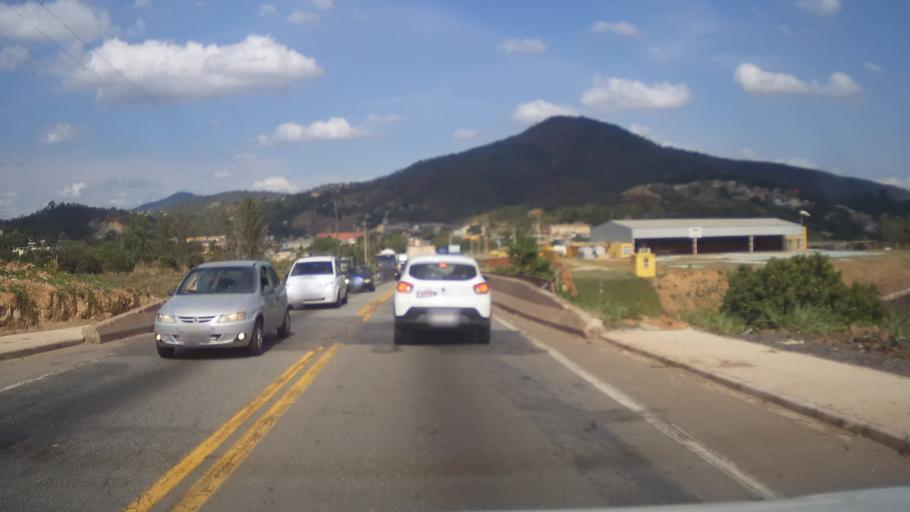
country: BR
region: Minas Gerais
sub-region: Santa Luzia
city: Santa Luzia
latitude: -19.8405
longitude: -43.8725
